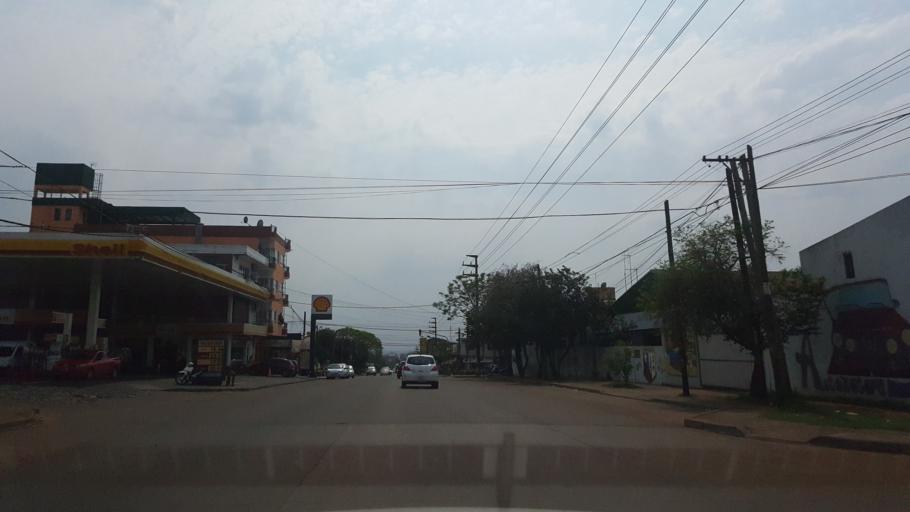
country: AR
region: Misiones
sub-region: Departamento de Capital
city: Posadas
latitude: -27.3907
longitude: -55.9122
